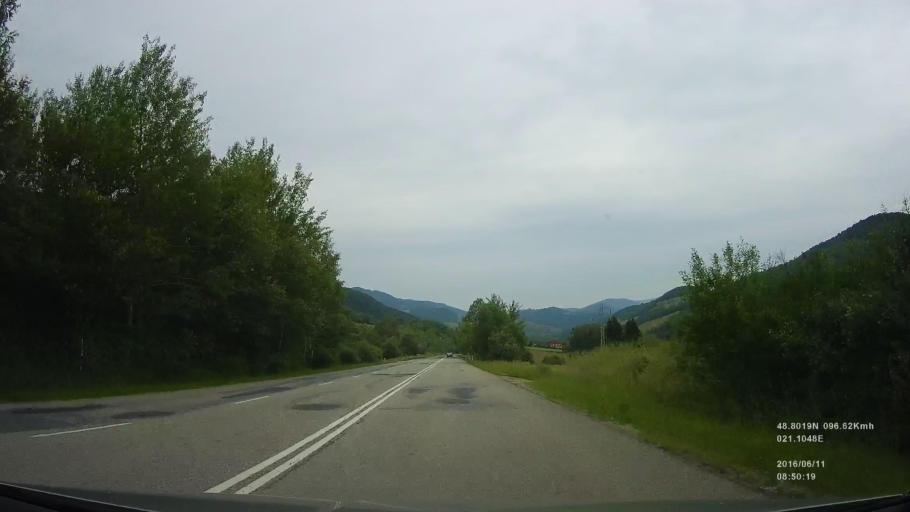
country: SK
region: Kosicky
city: Kosice
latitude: 48.7965
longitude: 21.1142
